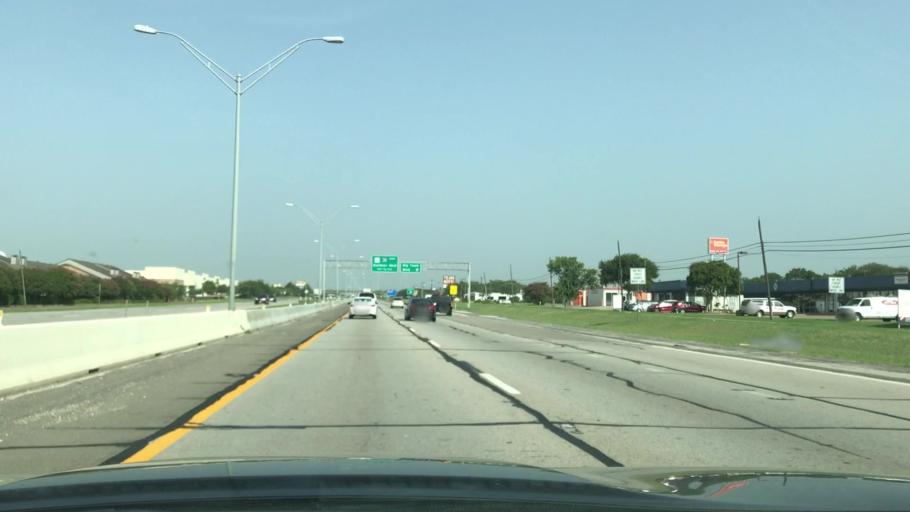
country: US
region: Texas
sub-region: Dallas County
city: Mesquite
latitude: 32.7950
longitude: -96.6607
